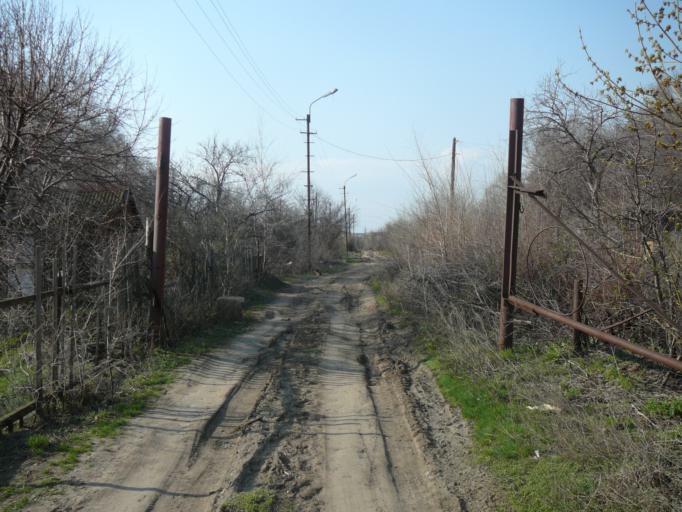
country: RU
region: Saratov
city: Engel's
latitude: 51.4579
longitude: 46.1686
